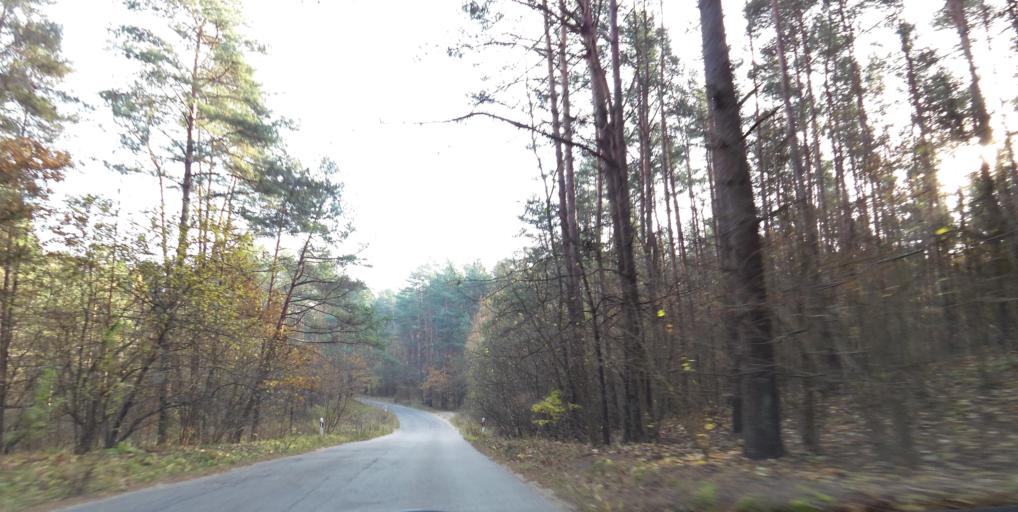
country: LT
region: Vilnius County
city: Pilaite
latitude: 54.6965
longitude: 25.1955
